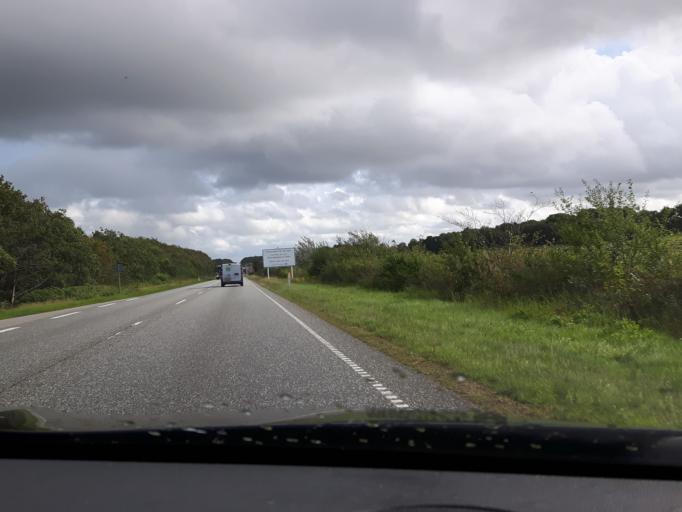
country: DK
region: Central Jutland
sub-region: Herning Kommune
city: Avlum
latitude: 56.2977
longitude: 8.7205
